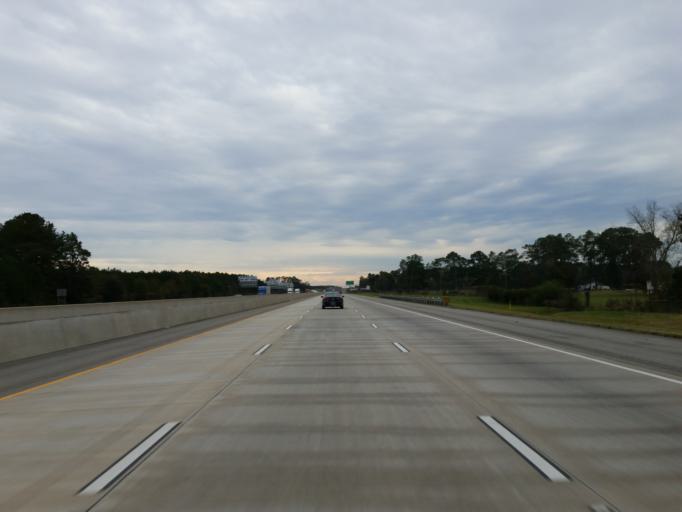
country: US
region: Georgia
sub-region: Cook County
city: Sparks
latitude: 31.2307
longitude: -83.4635
